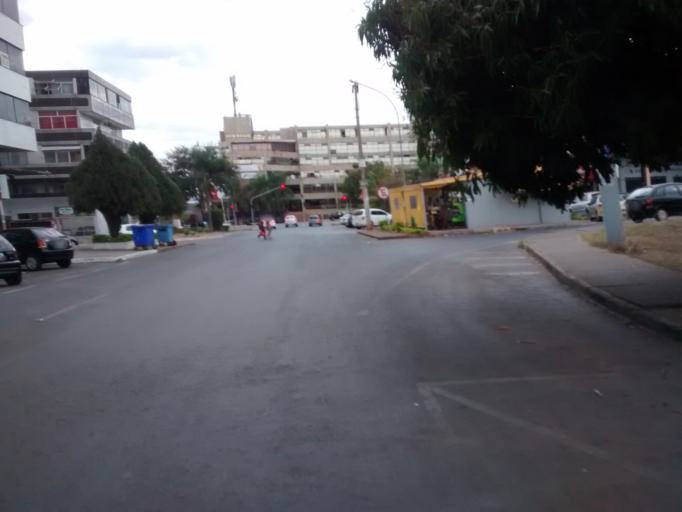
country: BR
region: Federal District
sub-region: Brasilia
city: Brasilia
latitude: -15.7393
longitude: -47.9002
